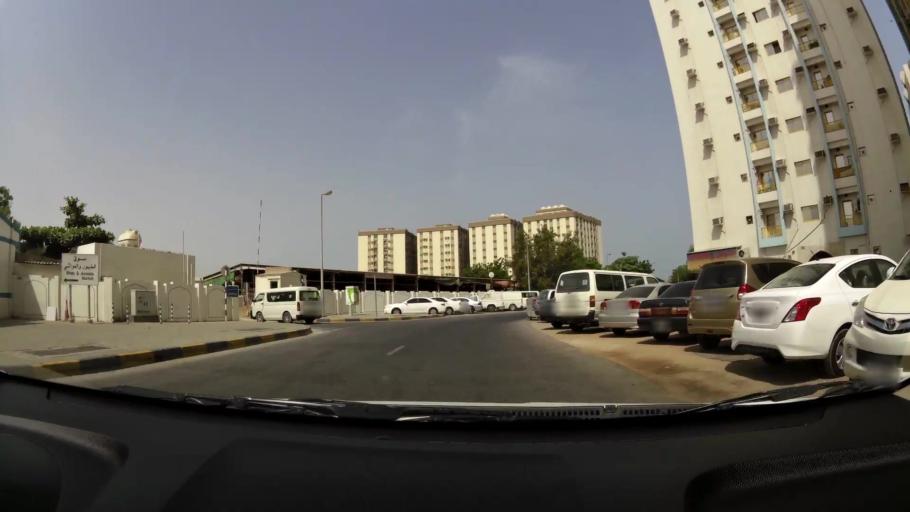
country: AE
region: Ash Shariqah
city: Sharjah
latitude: 25.3556
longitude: 55.3805
